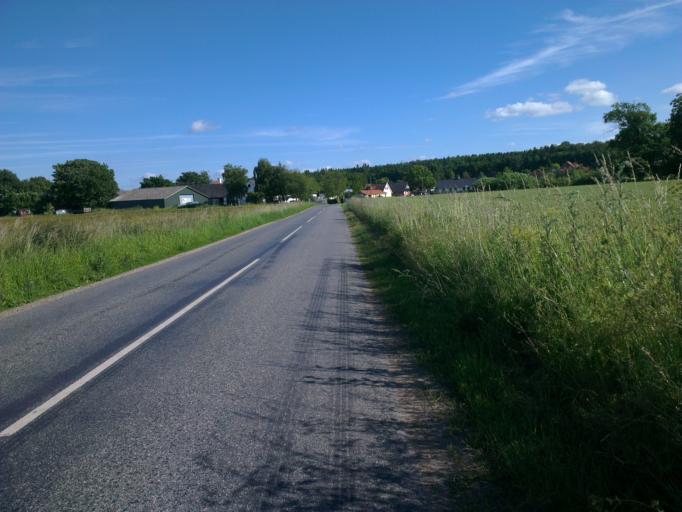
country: DK
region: Capital Region
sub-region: Frederikssund Kommune
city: Skibby
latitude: 55.7968
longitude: 11.9537
